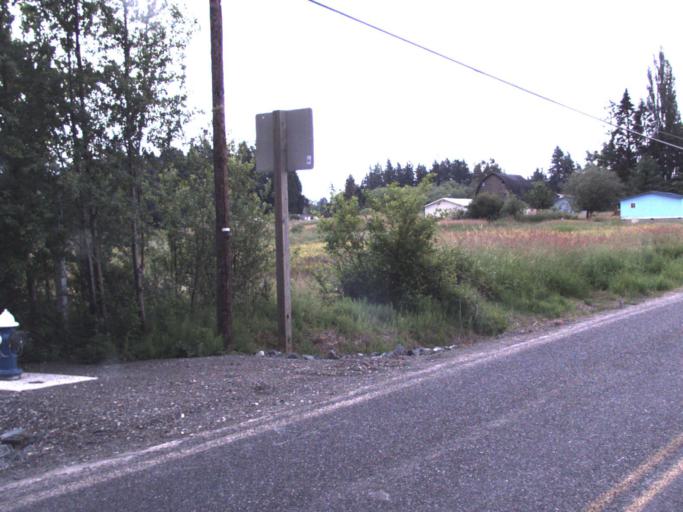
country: US
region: Washington
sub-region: Whatcom County
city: Birch Bay
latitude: 48.9522
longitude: -122.7261
